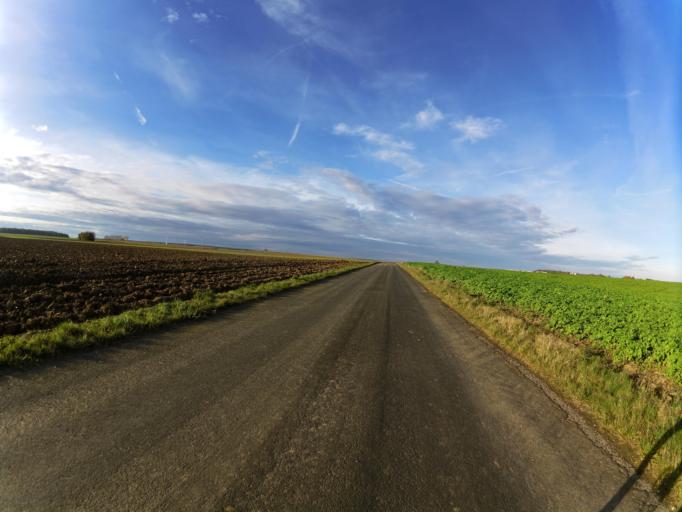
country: DE
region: Bavaria
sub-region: Regierungsbezirk Unterfranken
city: Giebelstadt
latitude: 49.6684
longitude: 9.9407
